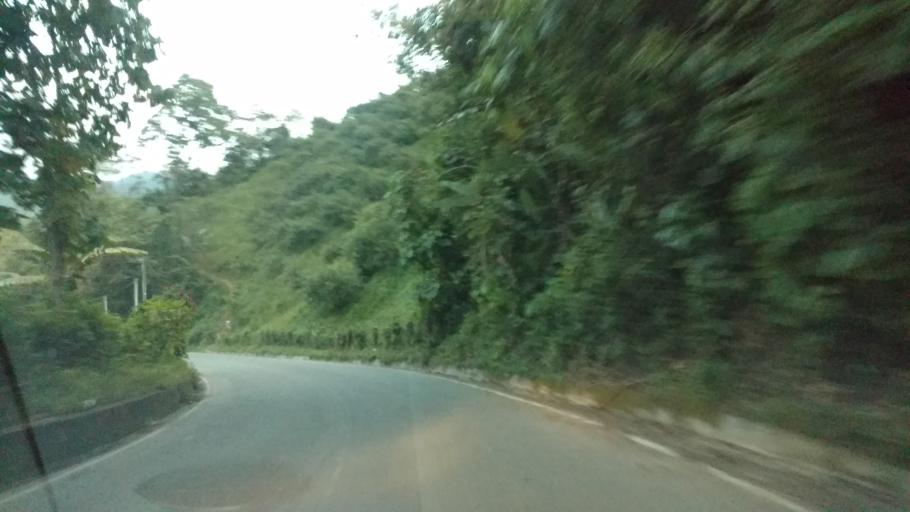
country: CO
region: Caldas
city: Aranzazu
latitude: 5.2599
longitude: -75.4989
